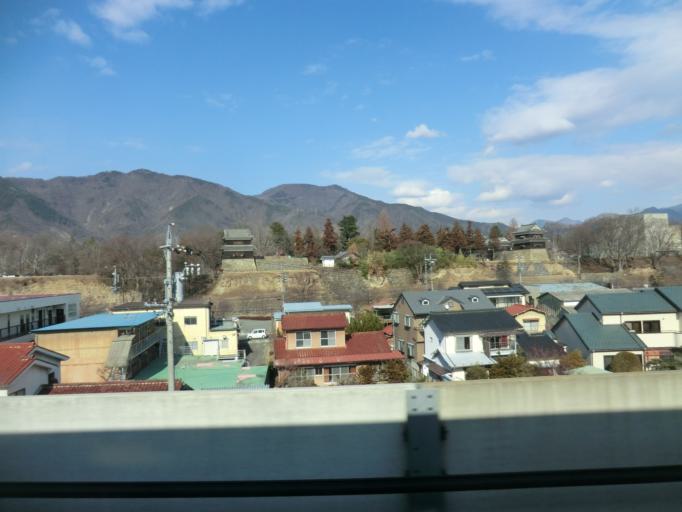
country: JP
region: Nagano
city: Ueda
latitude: 36.4020
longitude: 138.2427
